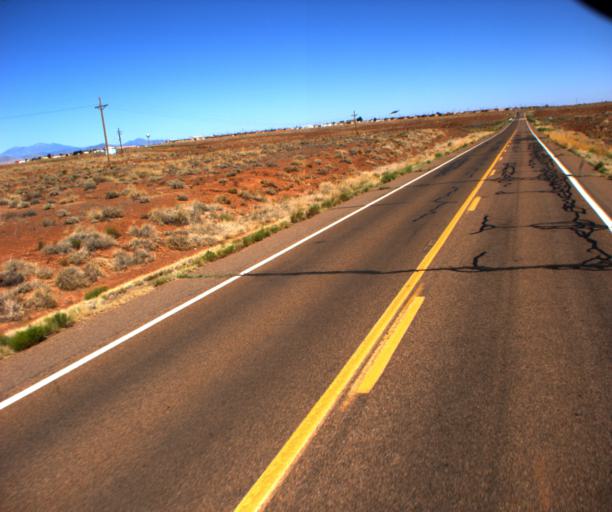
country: US
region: Arizona
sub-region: Coconino County
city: LeChee
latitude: 35.2923
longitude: -110.9884
